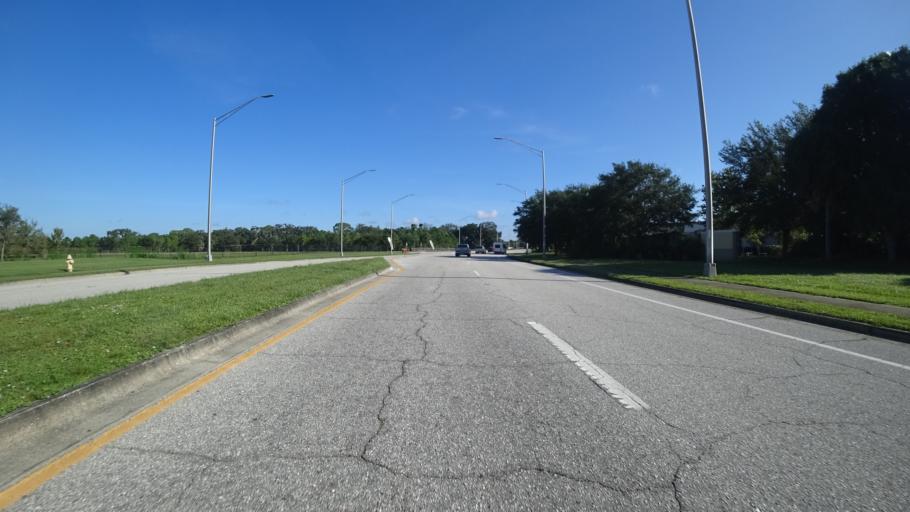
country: US
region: Florida
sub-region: Manatee County
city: Ellenton
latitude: 27.4959
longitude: -82.4843
